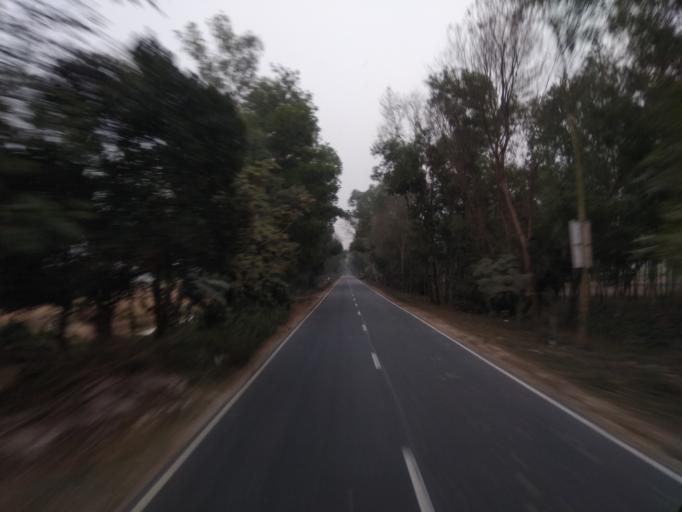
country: BD
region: Rajshahi
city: Bogra
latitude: 24.6555
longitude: 89.2628
